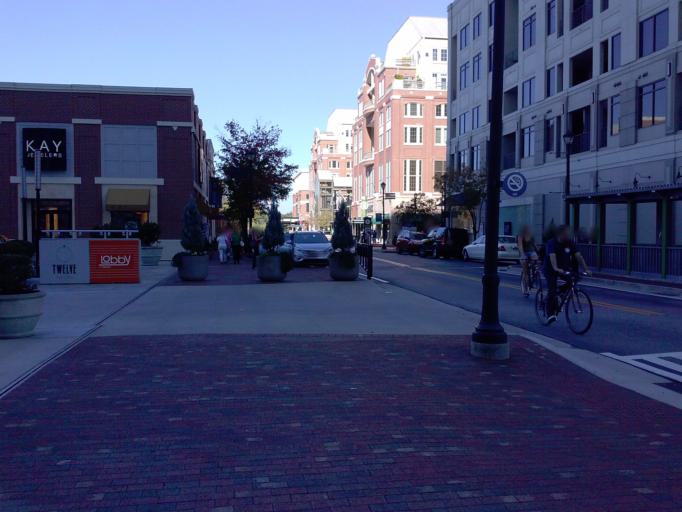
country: US
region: Georgia
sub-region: Fulton County
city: Atlanta
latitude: 33.7917
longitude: -84.3976
